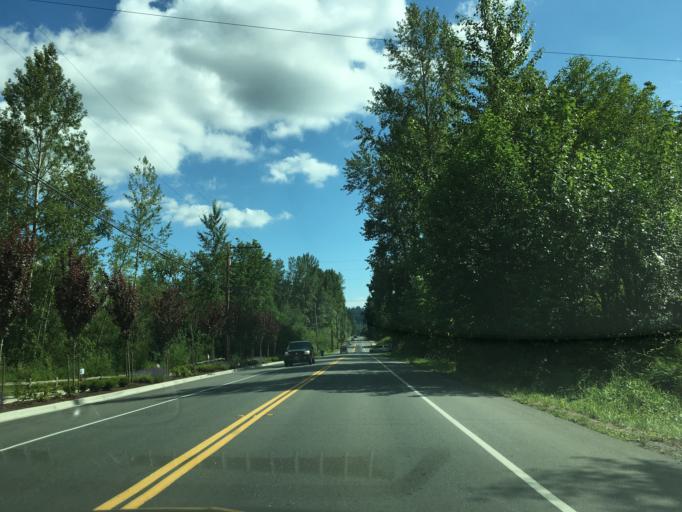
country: US
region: Washington
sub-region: King County
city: Kenmore
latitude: 47.7708
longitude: -122.2332
